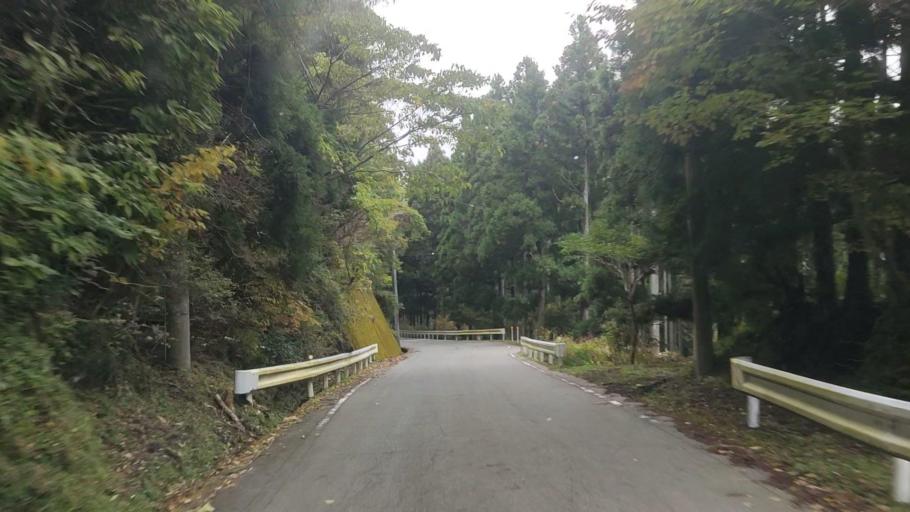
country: JP
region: Shizuoka
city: Heda
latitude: 34.9246
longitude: 138.8450
